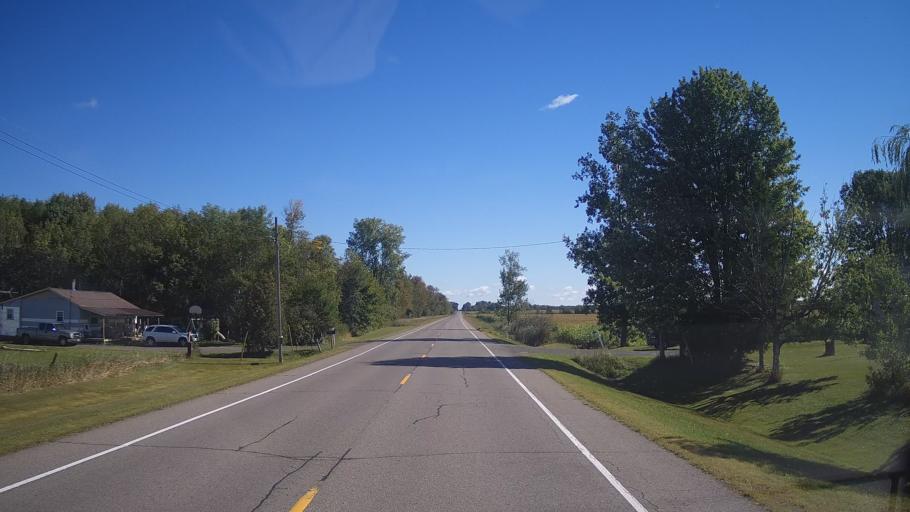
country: CA
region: Ontario
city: Prescott
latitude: 44.9306
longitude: -75.3311
